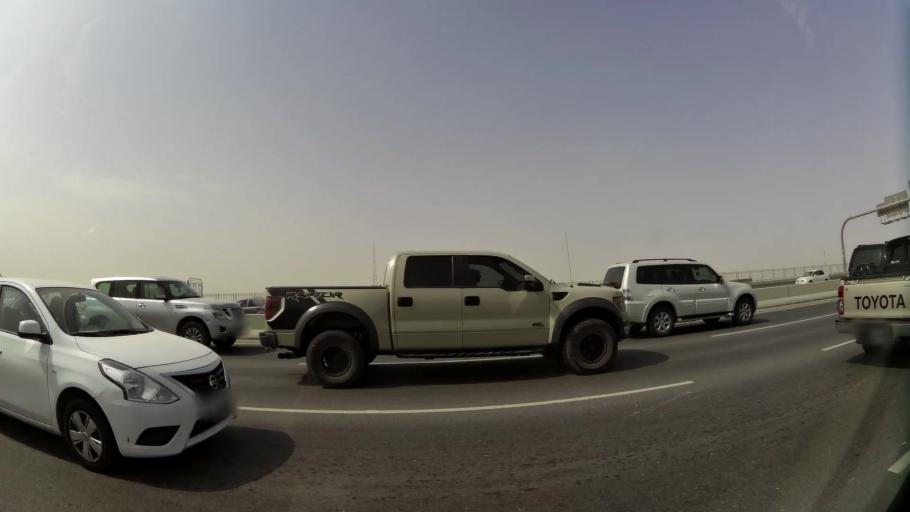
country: QA
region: Baladiyat ad Dawhah
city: Doha
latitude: 25.2901
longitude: 51.4780
